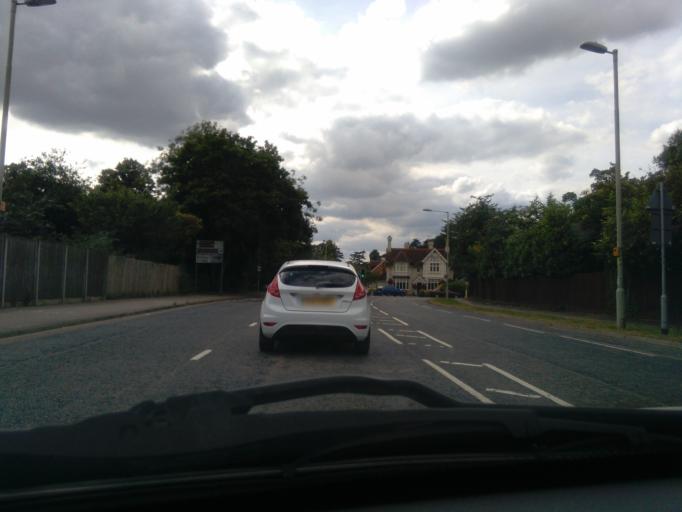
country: GB
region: England
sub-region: Bedford
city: Bedford
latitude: 52.1469
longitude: -0.4544
